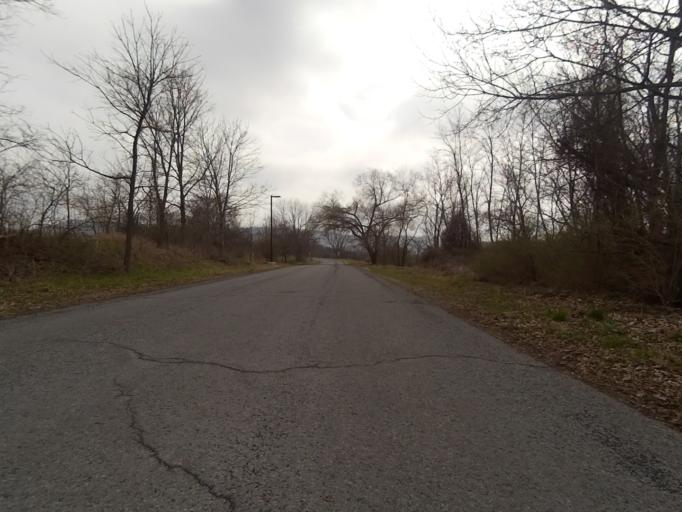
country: US
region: Pennsylvania
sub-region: Centre County
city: Boalsburg
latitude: 40.7922
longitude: -77.7971
